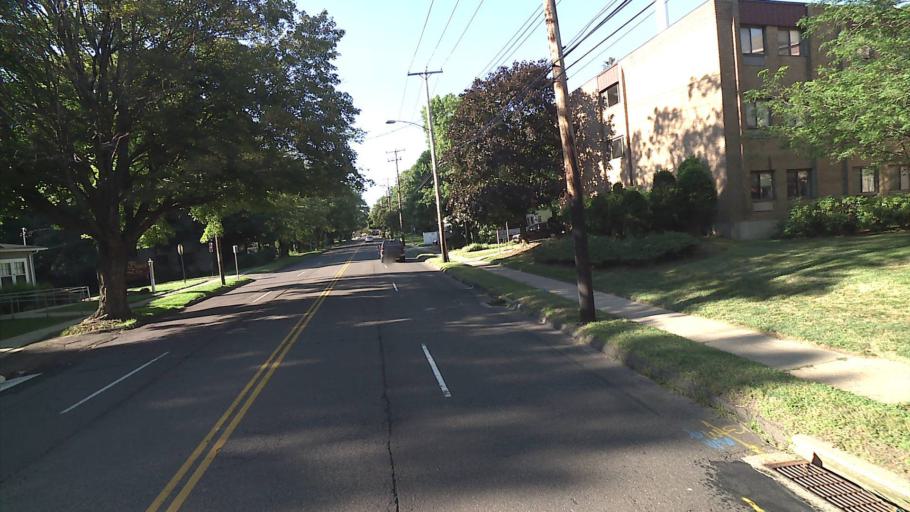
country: US
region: Connecticut
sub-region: New Haven County
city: Hamden
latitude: 41.3982
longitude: -72.8973
